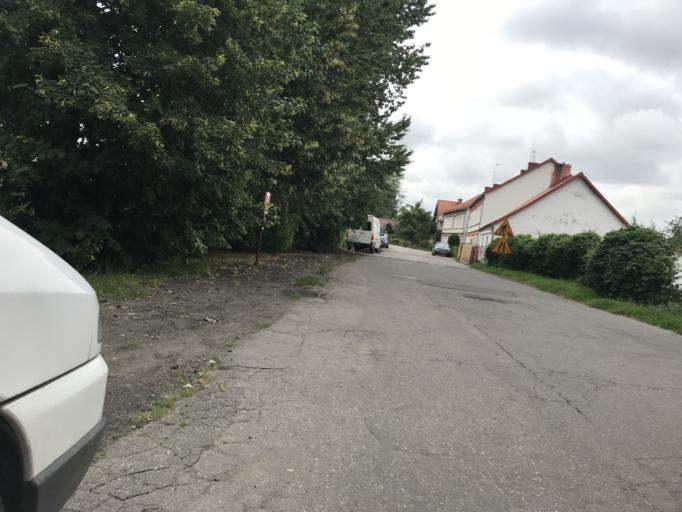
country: PL
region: Warmian-Masurian Voivodeship
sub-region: Powiat elblaski
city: Elblag
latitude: 54.1560
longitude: 19.3877
